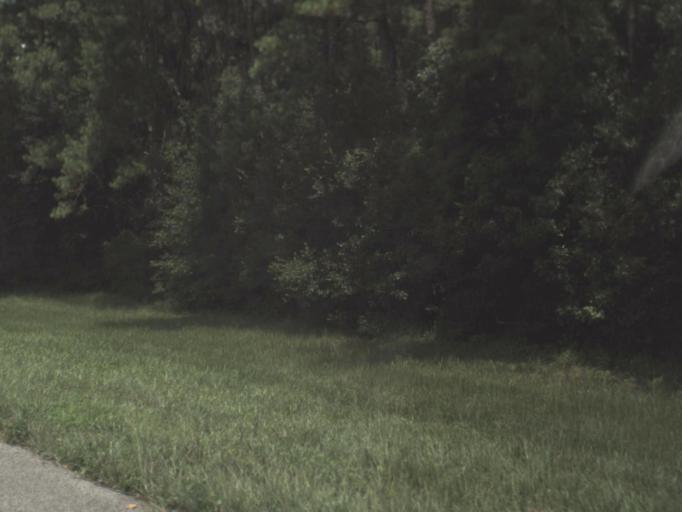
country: US
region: Florida
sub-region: Hernando County
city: North Brooksville
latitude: 28.5995
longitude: -82.4007
